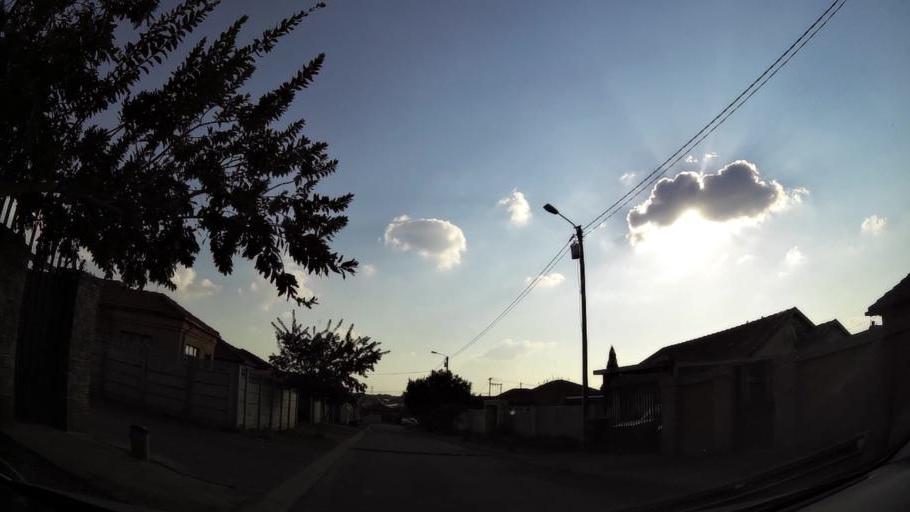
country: ZA
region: Gauteng
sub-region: Ekurhuleni Metropolitan Municipality
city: Tembisa
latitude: -25.9514
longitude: 28.2103
